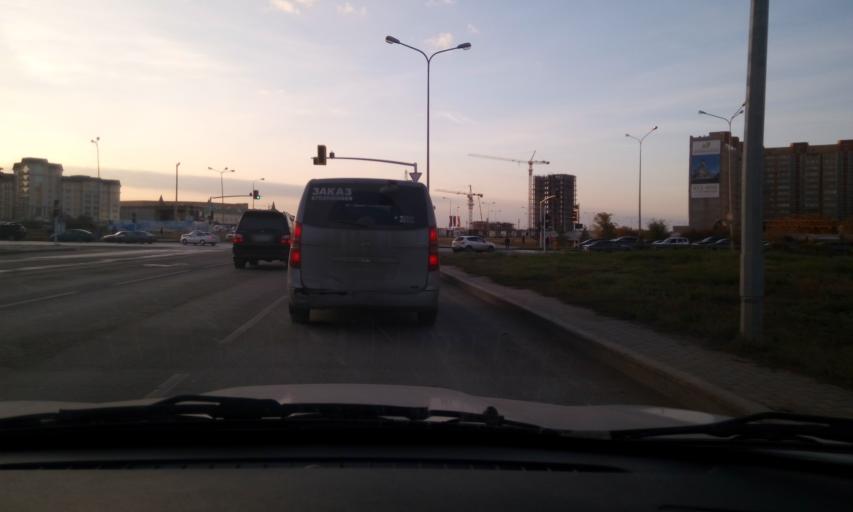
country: KZ
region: Astana Qalasy
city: Astana
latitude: 51.1267
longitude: 71.4861
